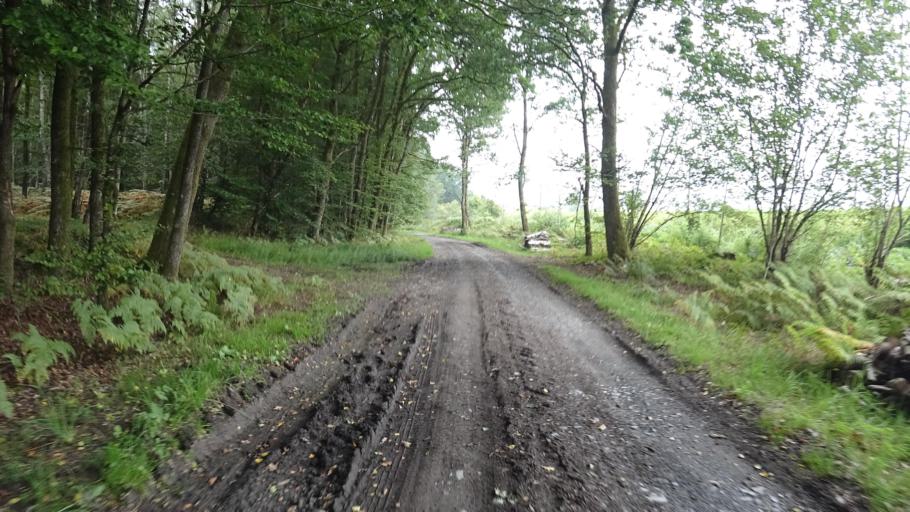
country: BE
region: Wallonia
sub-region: Province du Luxembourg
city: Chiny
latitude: 49.8027
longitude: 5.3287
